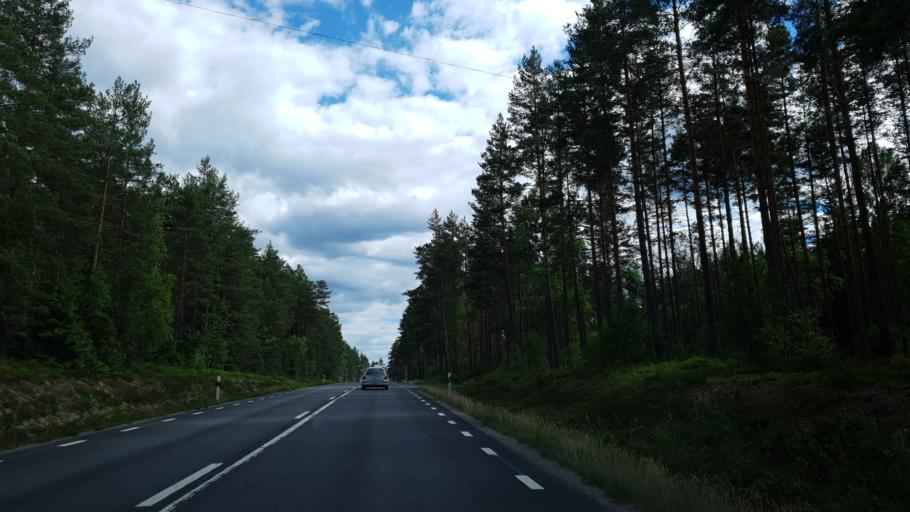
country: SE
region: Kronoberg
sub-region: Lessebo Kommun
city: Lessebo
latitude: 56.8215
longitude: 15.4072
